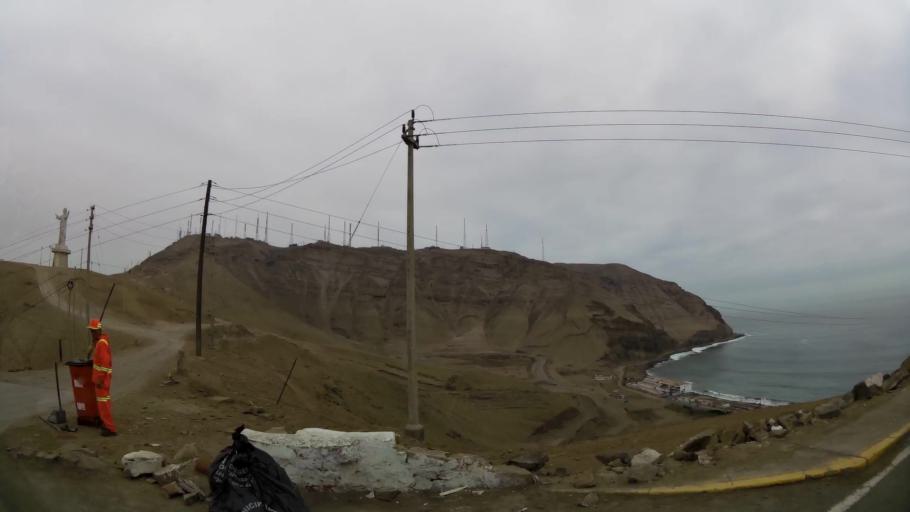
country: PE
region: Lima
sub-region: Lima
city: Surco
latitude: -12.1725
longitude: -77.0304
